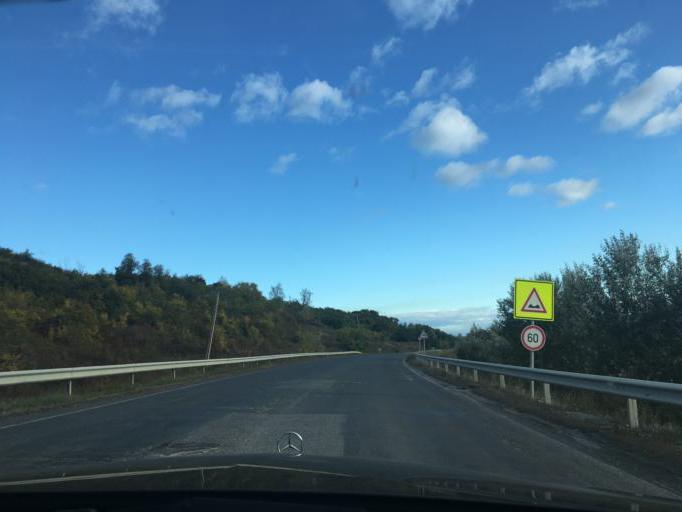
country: HU
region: Borsod-Abauj-Zemplen
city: Gonc
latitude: 48.4869
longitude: 21.2117
